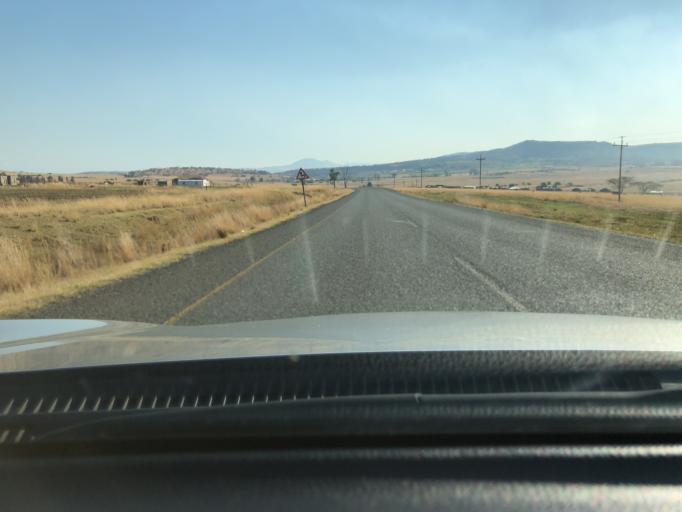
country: ZA
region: KwaZulu-Natal
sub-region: uThukela District Municipality
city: Ekuvukeni
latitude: -28.3334
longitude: 30.0522
